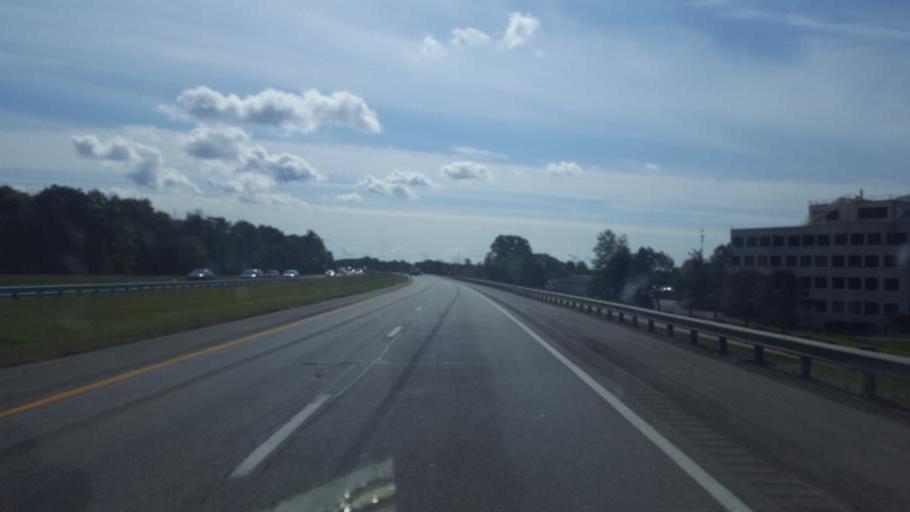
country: US
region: Ohio
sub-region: Cuyahoga County
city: Solon
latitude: 41.4057
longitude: -81.4666
